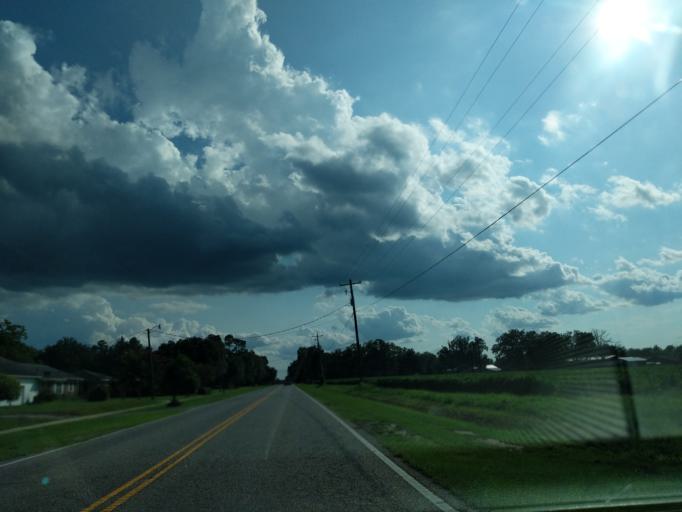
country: US
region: South Carolina
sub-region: Barnwell County
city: Williston
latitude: 33.4145
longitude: -81.4072
